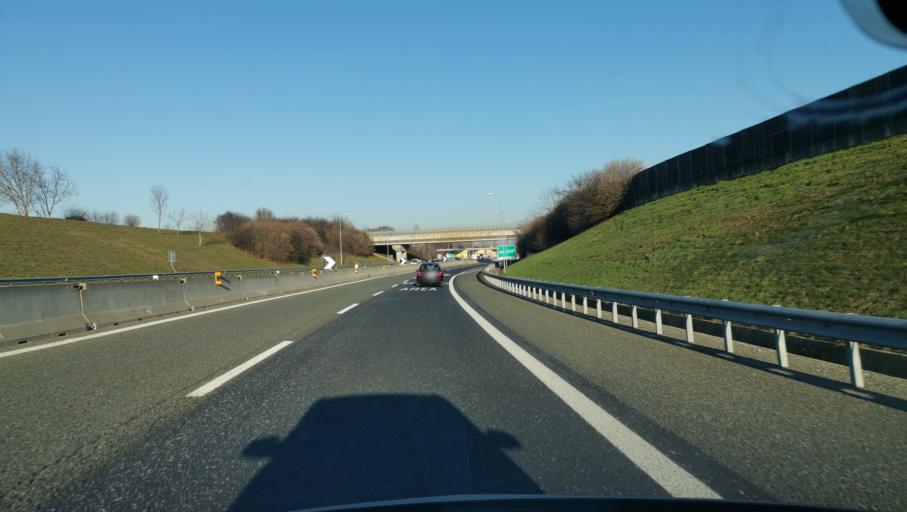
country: IT
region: Piedmont
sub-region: Provincia di Torino
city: Piscina
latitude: 44.9048
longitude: 7.4246
